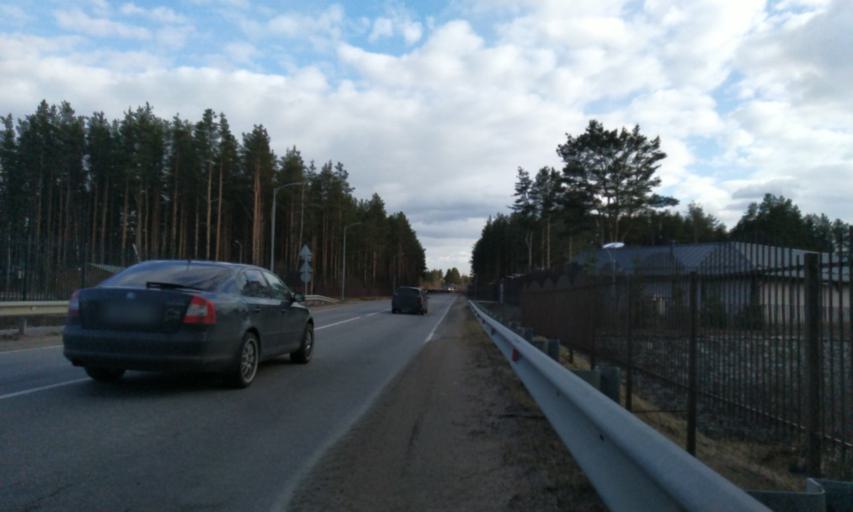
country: RU
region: Leningrad
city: Novoye Devyatkino
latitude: 60.1171
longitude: 30.4494
